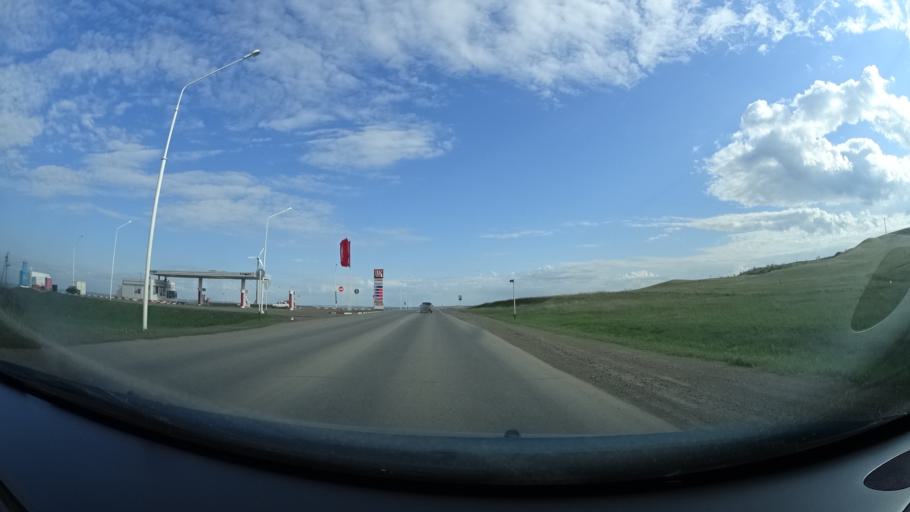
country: RU
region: Bashkortostan
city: Blagoveshchensk
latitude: 55.1759
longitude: 55.8538
